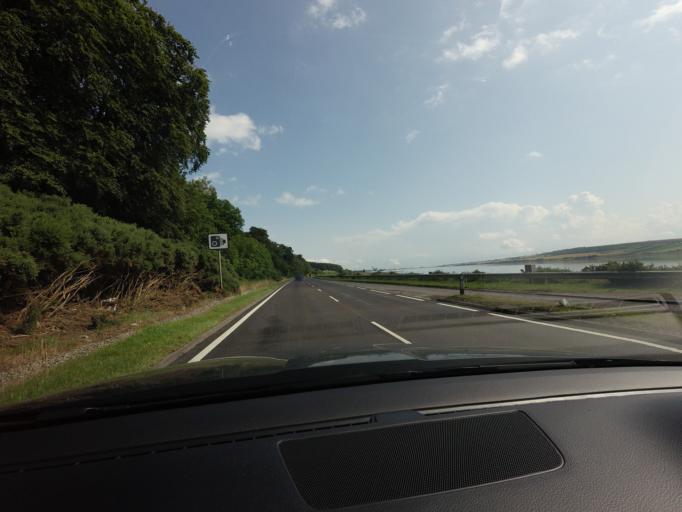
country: GB
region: Scotland
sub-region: Highland
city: Evanton
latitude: 57.6324
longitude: -4.3641
